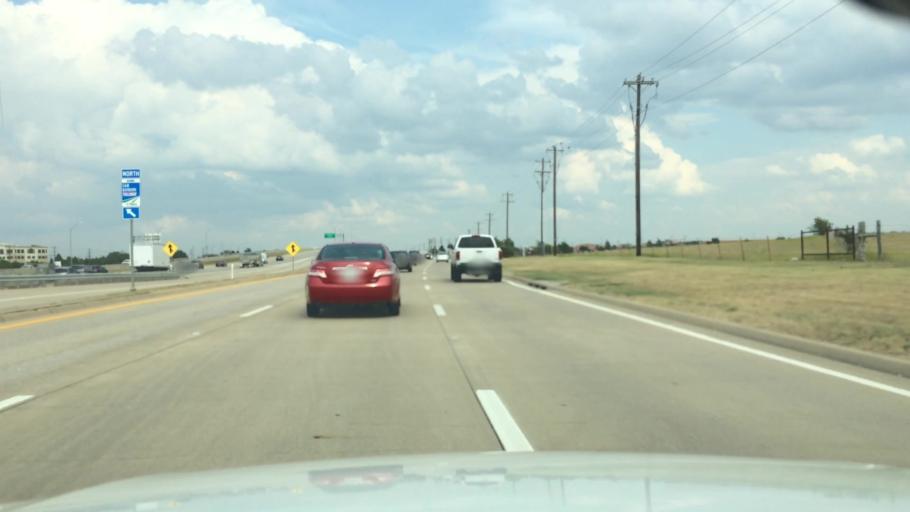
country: US
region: Texas
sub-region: Collin County
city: Frisco
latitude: 33.1092
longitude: -96.7746
